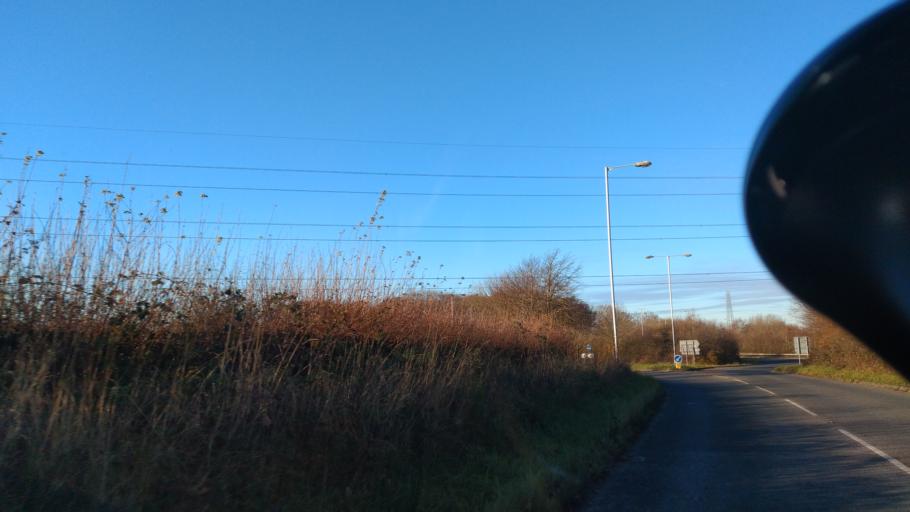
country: GB
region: England
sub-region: Somerset
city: Frome
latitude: 51.2401
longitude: -2.2872
